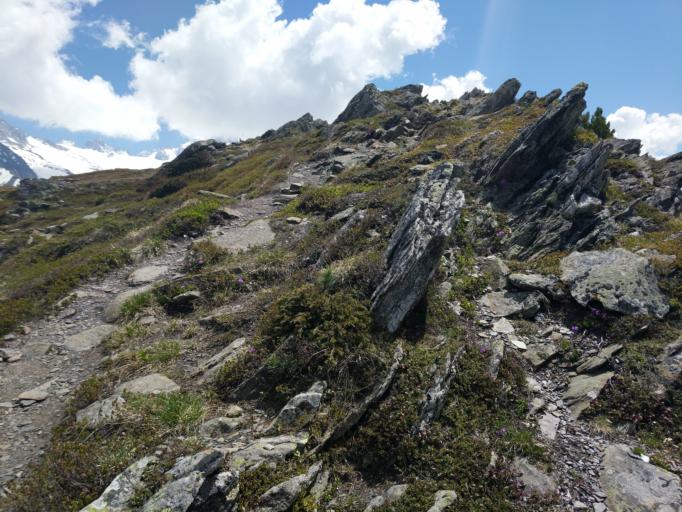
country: FR
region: Rhone-Alpes
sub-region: Departement de la Haute-Savoie
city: Chamonix-Mont-Blanc
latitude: 46.0187
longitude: 6.9395
